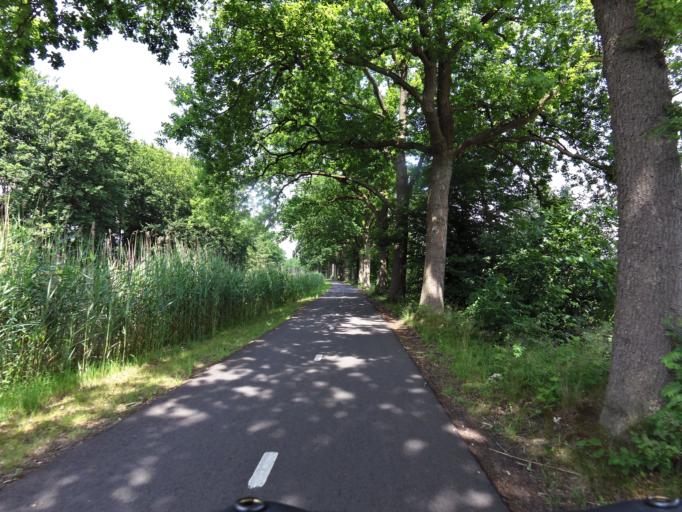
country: NL
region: Gelderland
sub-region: Gemeente Apeldoorn
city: Loenen
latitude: 52.1459
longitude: 6.0409
